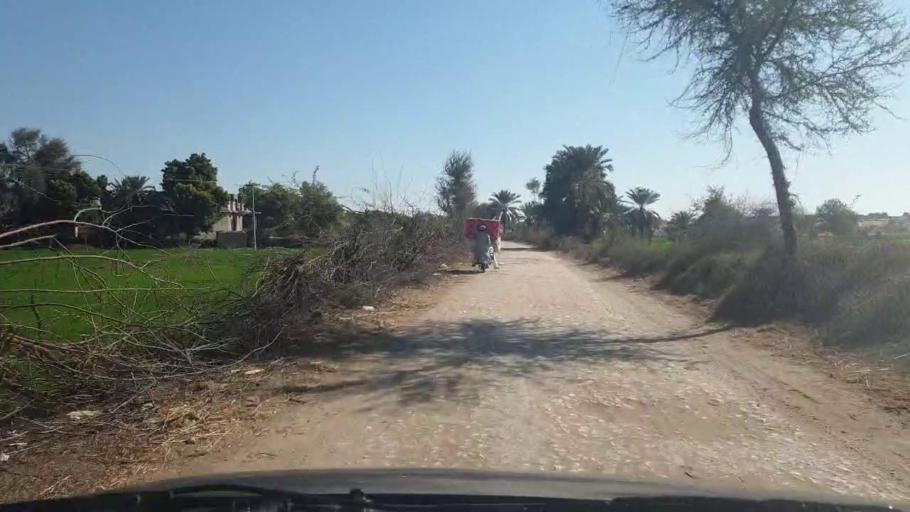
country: PK
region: Sindh
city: Bozdar
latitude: 27.0644
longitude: 68.6216
